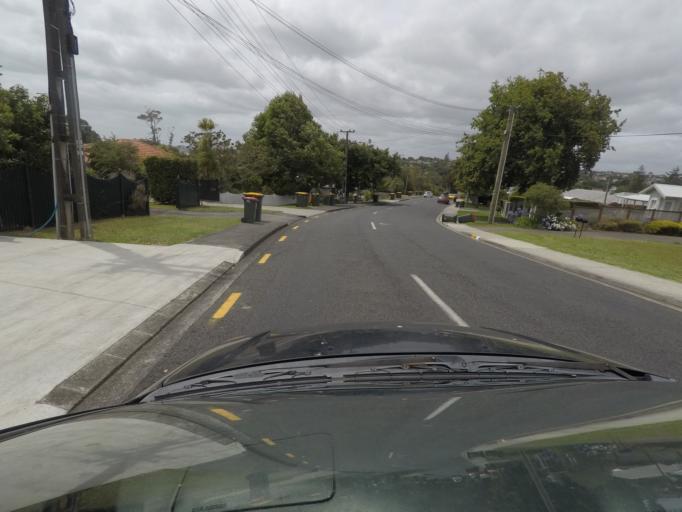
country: NZ
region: Auckland
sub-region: Auckland
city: Pakuranga
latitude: -36.8903
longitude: 174.9369
